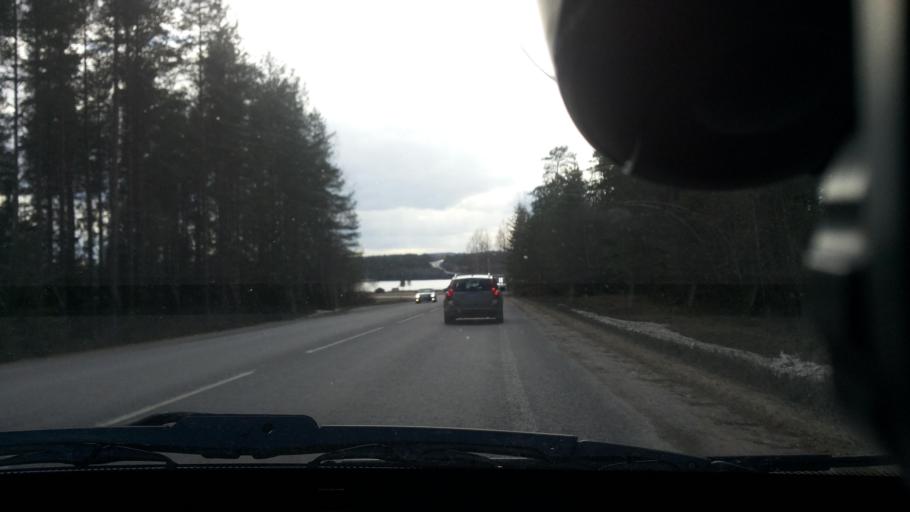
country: SE
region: Norrbotten
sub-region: Lulea Kommun
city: Gammelstad
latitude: 65.5945
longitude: 22.0470
